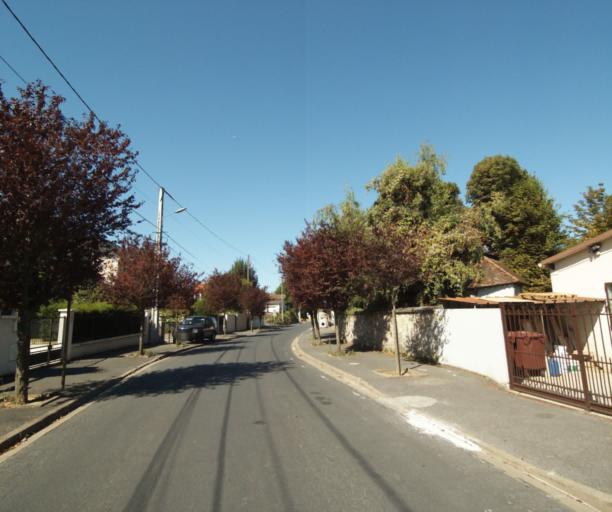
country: FR
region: Ile-de-France
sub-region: Departement de Seine-et-Marne
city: Lagny-sur-Marne
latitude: 48.8736
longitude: 2.7113
